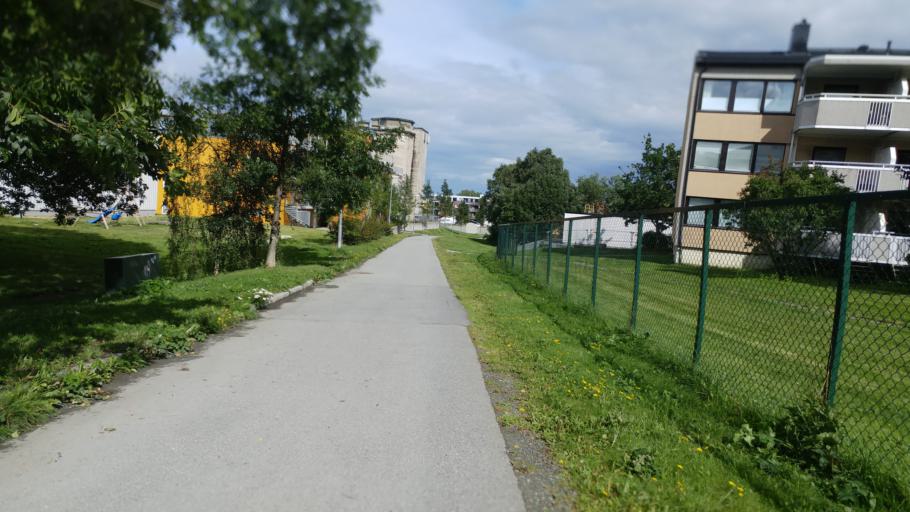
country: NO
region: Sor-Trondelag
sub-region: Trondheim
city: Trondheim
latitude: 63.4299
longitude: 10.4442
